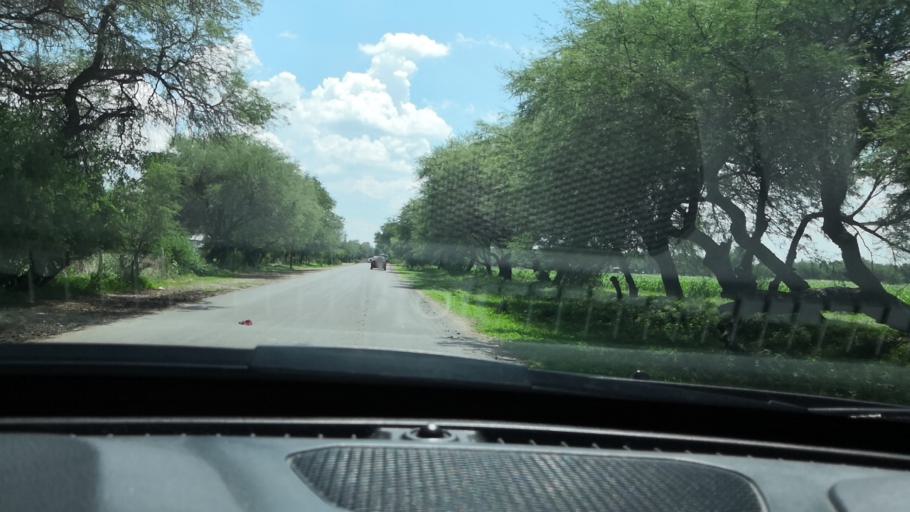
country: MX
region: Guanajuato
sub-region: Leon
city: Plan Guanajuato (La Sandia)
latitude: 20.9384
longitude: -101.6352
